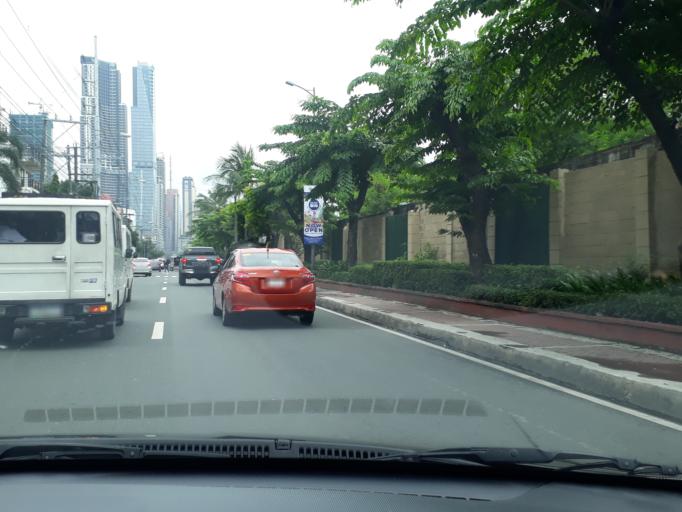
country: PH
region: Metro Manila
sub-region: Makati City
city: Makati City
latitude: 14.5680
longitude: 121.0199
